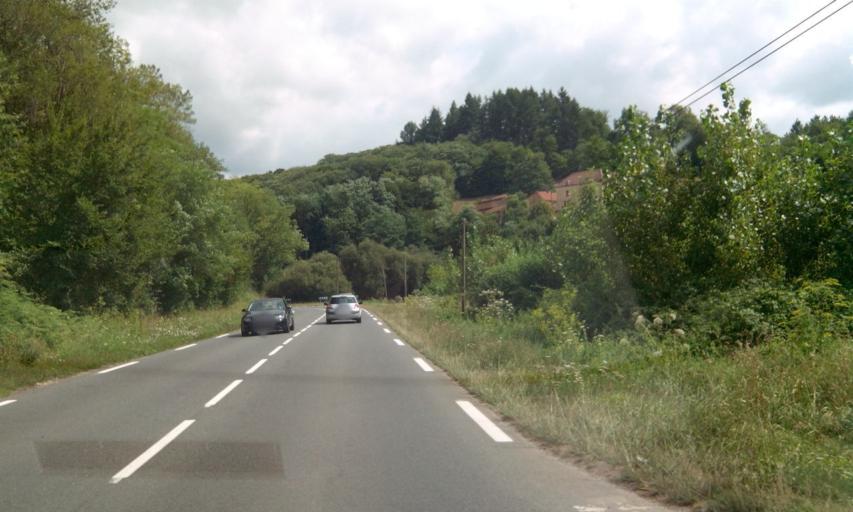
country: FR
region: Aquitaine
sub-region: Departement de la Dordogne
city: Carsac-Aillac
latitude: 44.8542
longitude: 1.3021
